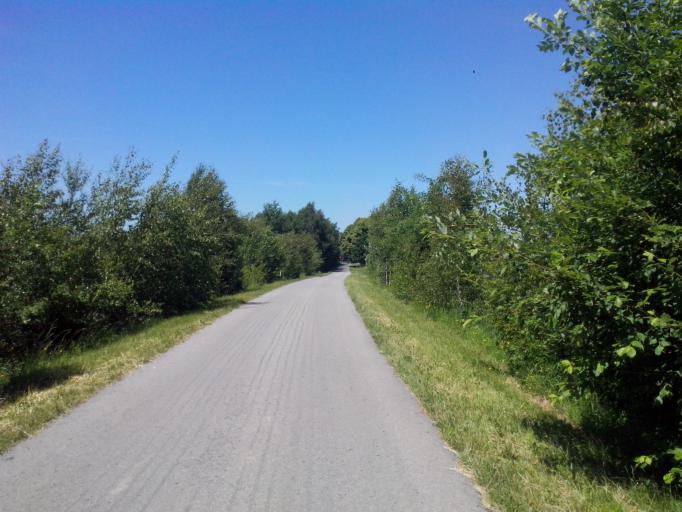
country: PL
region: Subcarpathian Voivodeship
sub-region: Powiat strzyzowski
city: Wysoka Strzyzowska
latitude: 49.8145
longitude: 21.7775
